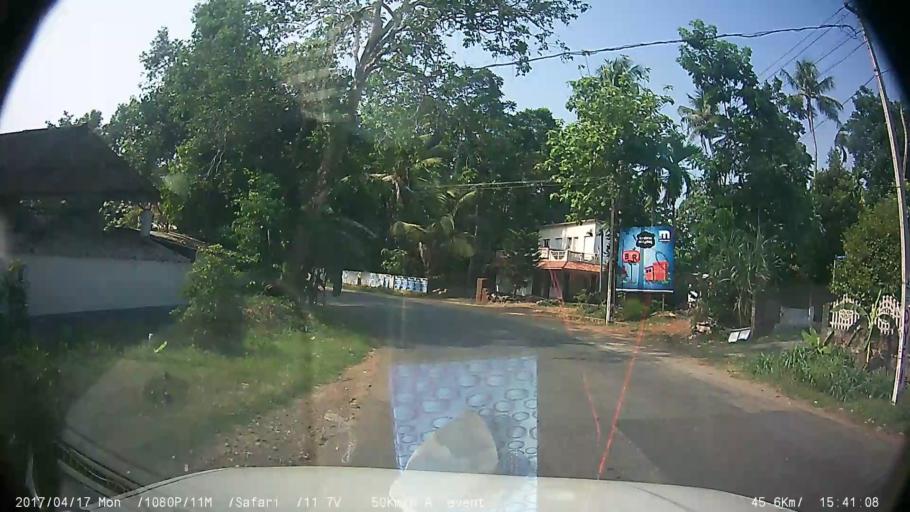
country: IN
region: Kerala
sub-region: Ernakulam
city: Ramamangalam
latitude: 10.0058
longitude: 76.4424
